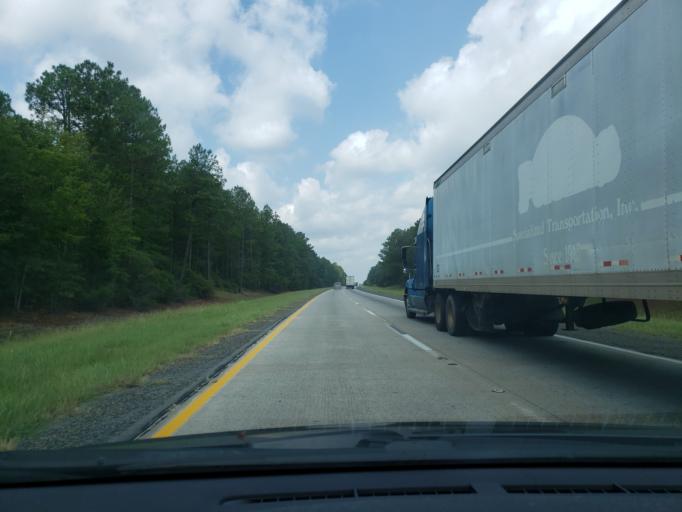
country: US
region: Georgia
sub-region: Treutlen County
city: Soperton
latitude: 32.4266
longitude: -82.5490
